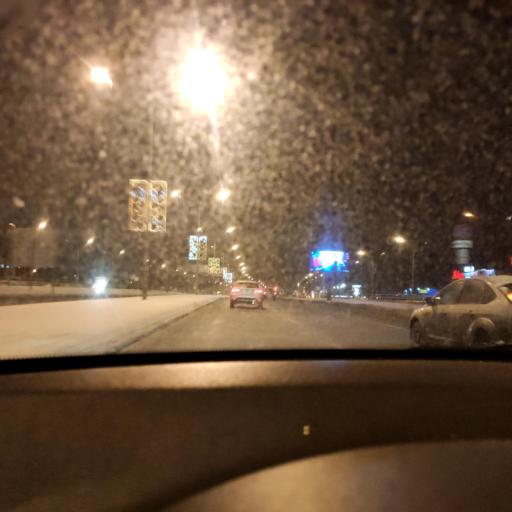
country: RU
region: Samara
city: Petra-Dubrava
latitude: 53.2818
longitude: 50.2788
